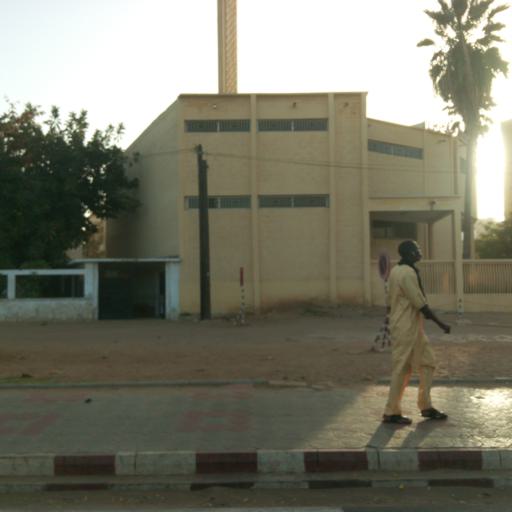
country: SN
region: Dakar
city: Dakar
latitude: 14.6923
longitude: -17.4476
